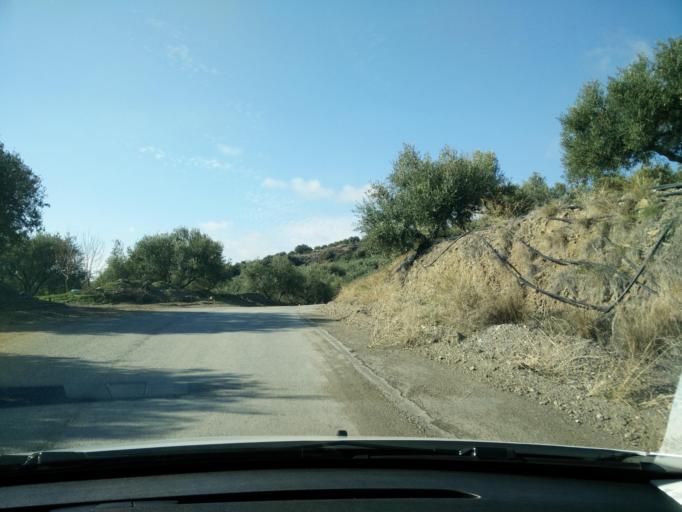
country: GR
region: Crete
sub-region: Nomos Lasithiou
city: Gra Liyia
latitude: 34.9991
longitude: 25.5192
